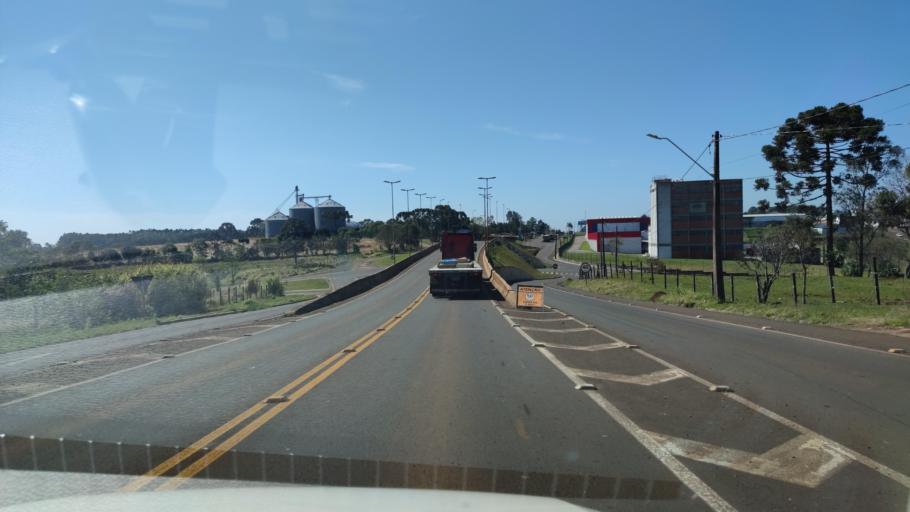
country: BR
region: Santa Catarina
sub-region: Sao Lourenco Do Oeste
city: Sao Lourenco dOeste
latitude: -26.3480
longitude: -52.8539
